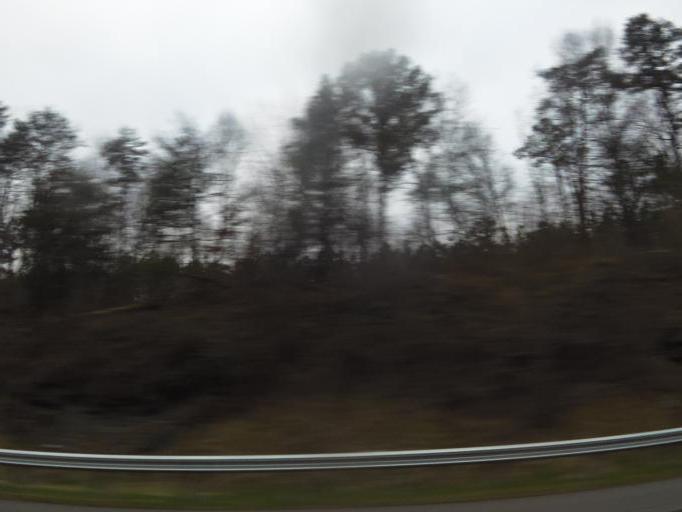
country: US
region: Alabama
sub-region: Jefferson County
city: Warrior
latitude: 33.8289
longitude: -86.8244
